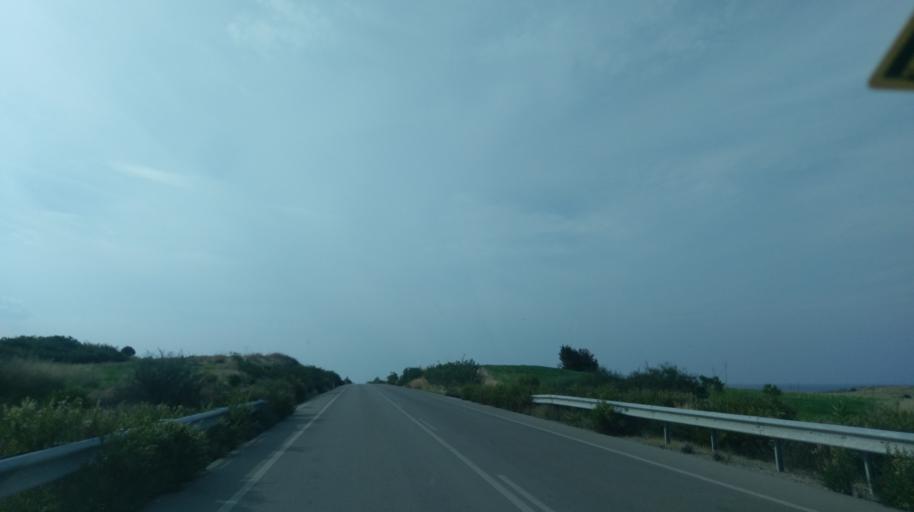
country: CY
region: Ammochostos
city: Trikomo
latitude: 35.4305
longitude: 33.9288
